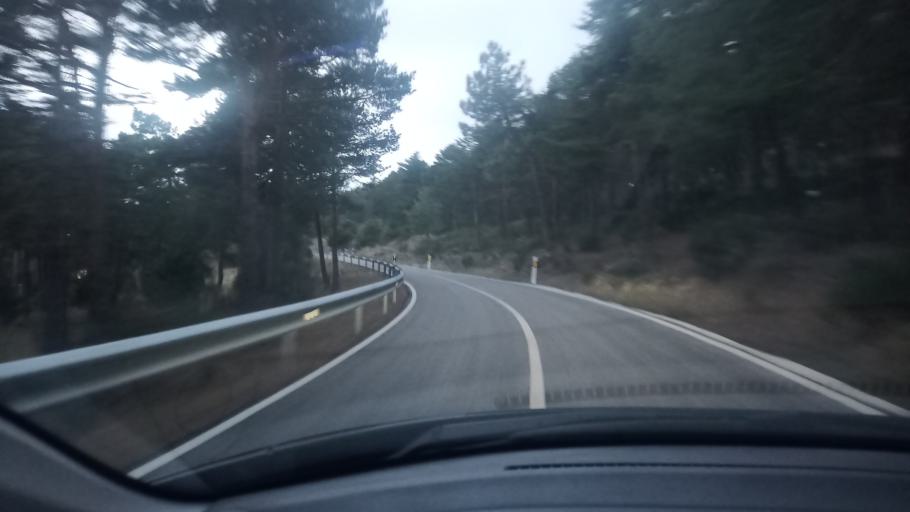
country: ES
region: Madrid
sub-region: Provincia de Madrid
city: Zarzalejo
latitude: 40.5544
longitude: -4.1918
